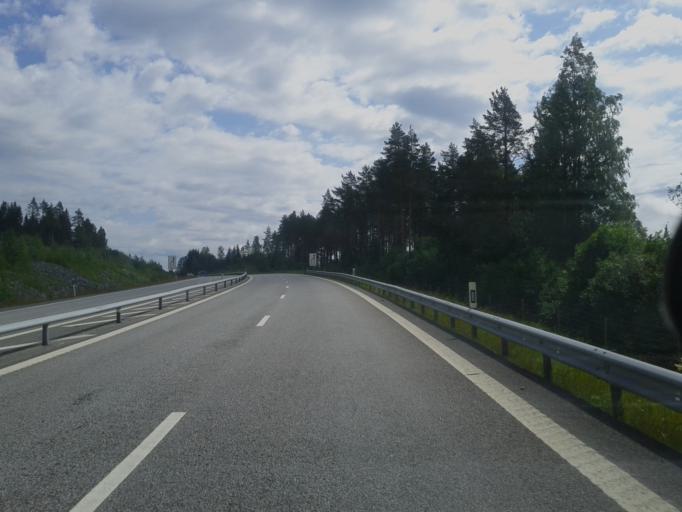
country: SE
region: Vaesternorrland
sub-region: OErnskoeldsviks Kommun
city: Ornskoldsvik
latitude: 63.2970
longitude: 18.8715
